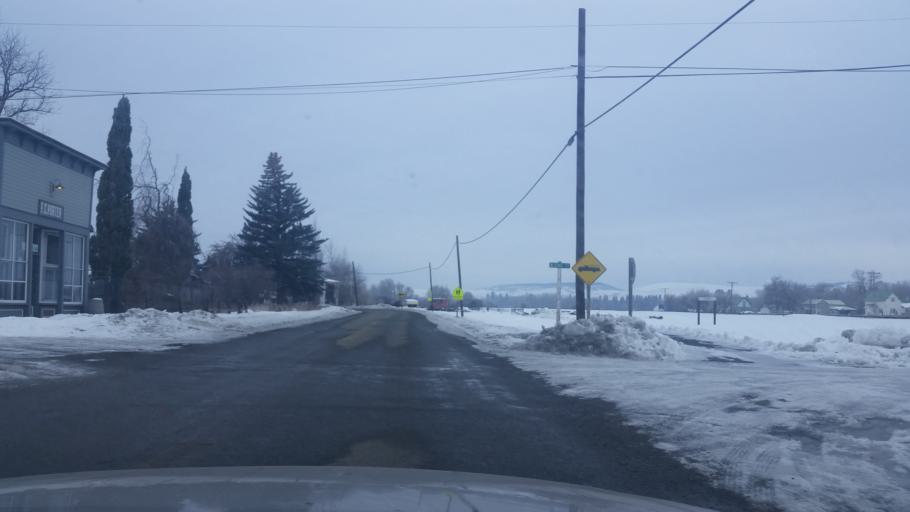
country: US
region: Washington
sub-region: Kittitas County
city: Ellensburg
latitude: 47.0687
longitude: -120.6709
